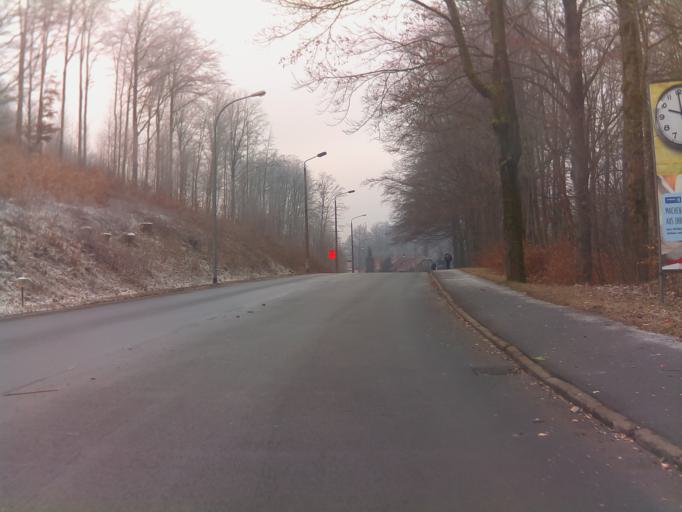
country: DE
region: Thuringia
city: Zella-Mehlis
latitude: 50.6648
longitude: 10.6842
